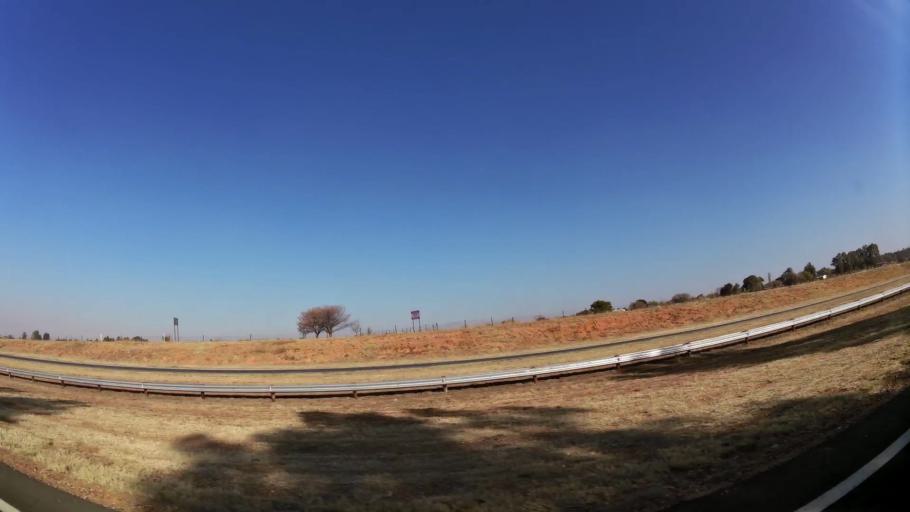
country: ZA
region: Gauteng
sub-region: West Rand District Municipality
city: Muldersdriseloop
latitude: -26.0082
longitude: 27.8914
